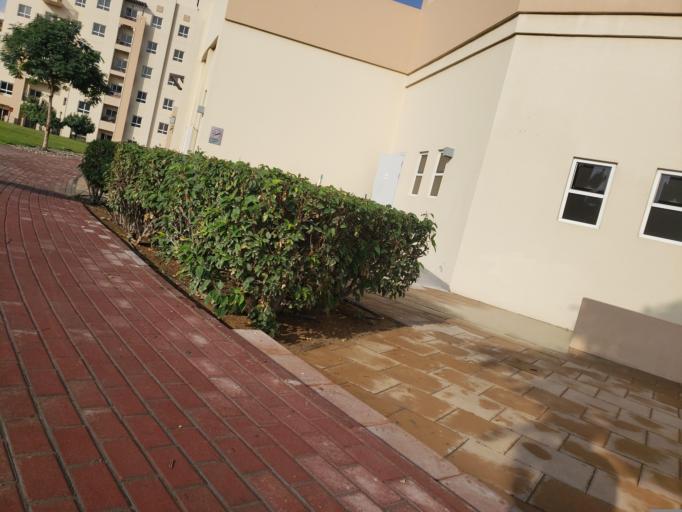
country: AE
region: Dubai
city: Dubai
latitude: 25.0018
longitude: 55.2530
